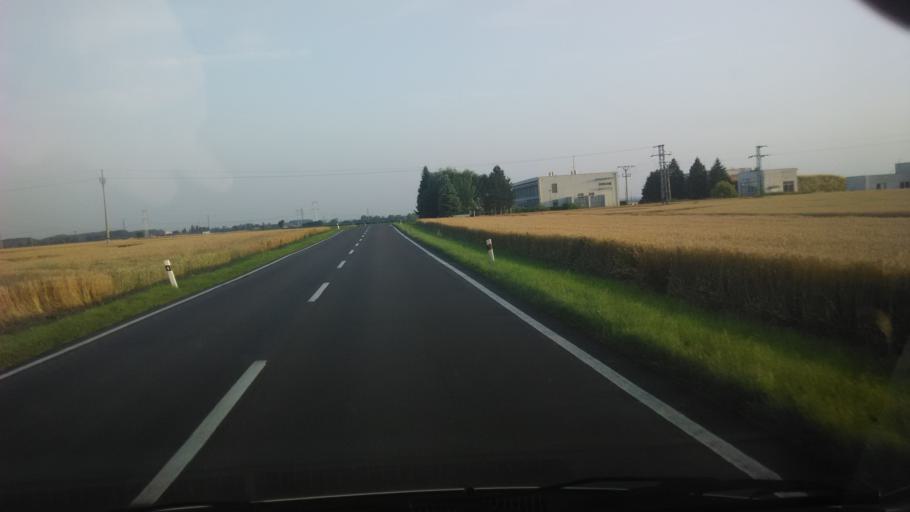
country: SK
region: Nitriansky
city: Tlmace
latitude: 48.2285
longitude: 18.5207
